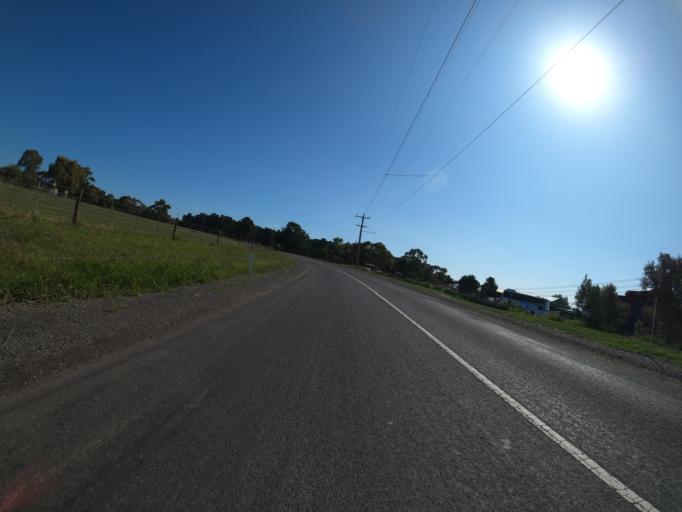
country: AU
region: Victoria
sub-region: Hume
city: Greenvale
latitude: -37.5471
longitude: 144.8703
